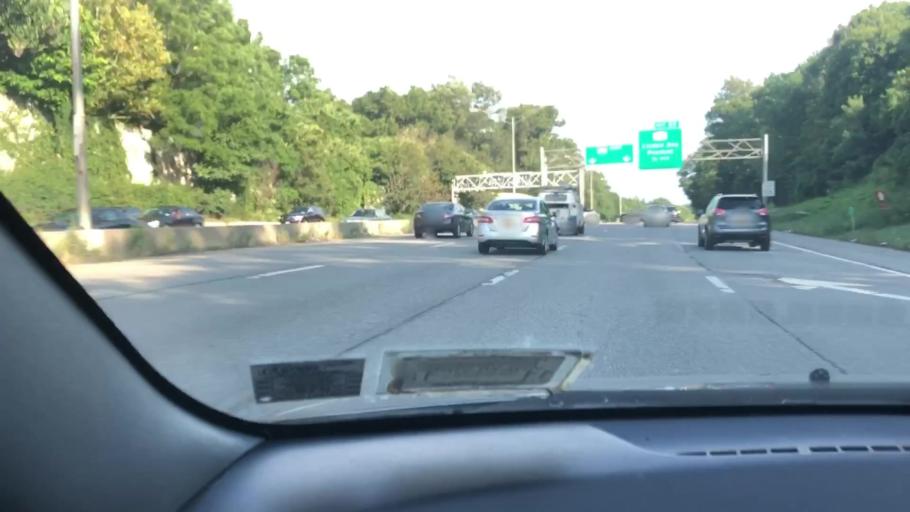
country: US
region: New York
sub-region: Monroe County
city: Brighton
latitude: 43.1351
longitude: -77.5352
